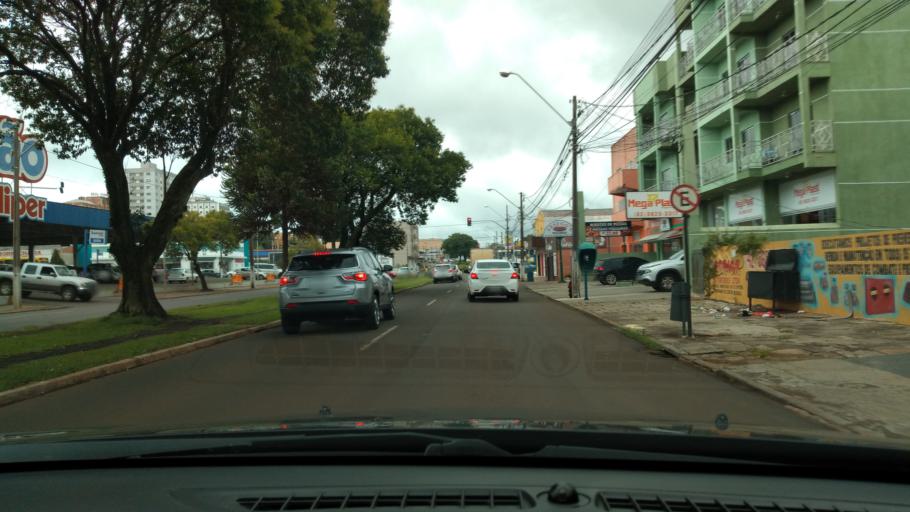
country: BR
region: Parana
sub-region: Guarapuava
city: Guarapuava
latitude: -25.3873
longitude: -51.4744
